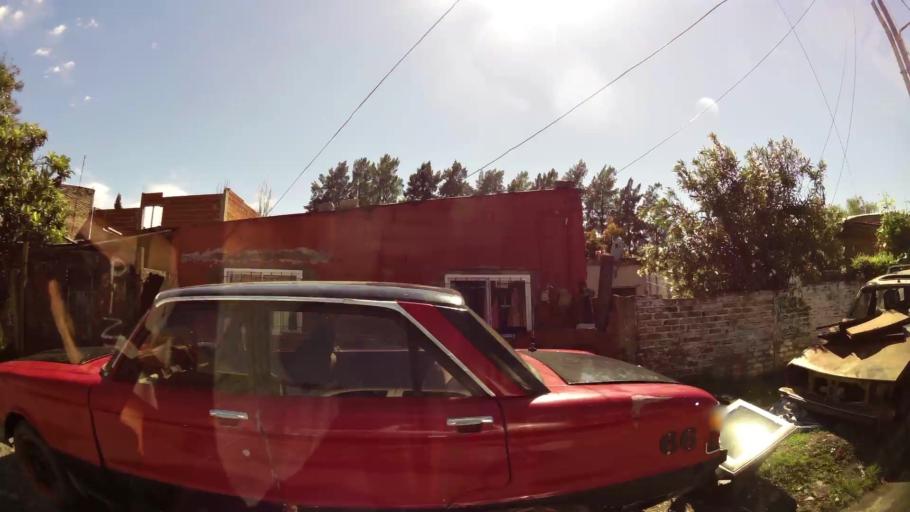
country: AR
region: Buenos Aires
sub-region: Partido de Avellaneda
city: Avellaneda
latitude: -34.6853
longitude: -58.3065
